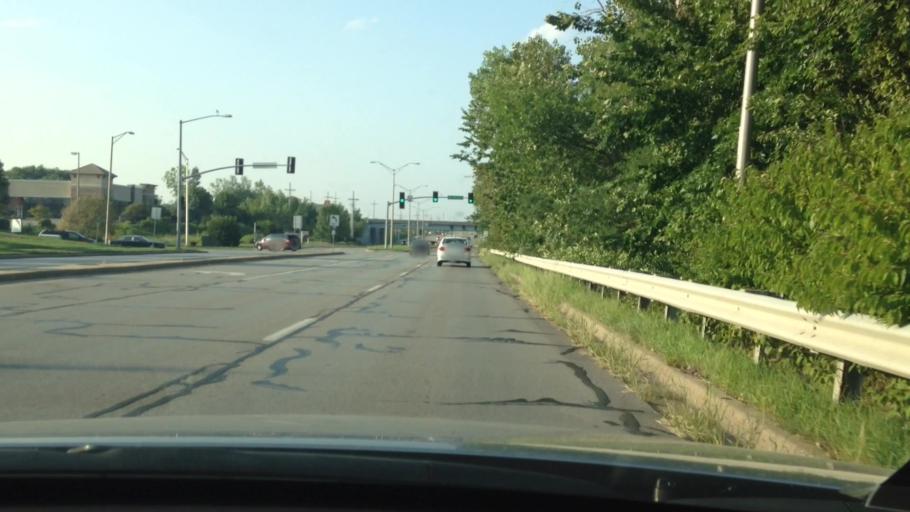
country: US
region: Missouri
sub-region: Platte County
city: Weatherby Lake
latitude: 39.2516
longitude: -94.6495
